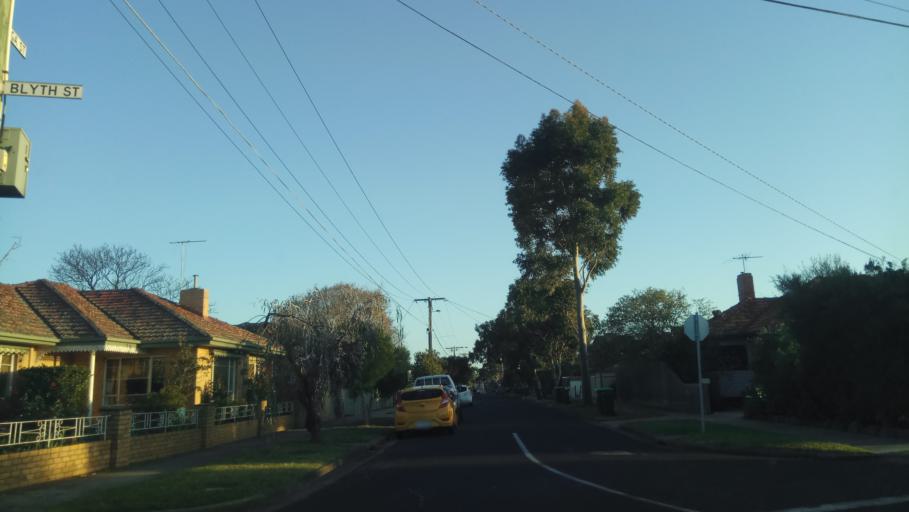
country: AU
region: Victoria
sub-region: Hobsons Bay
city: Altona
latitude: -37.8700
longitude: 144.8146
